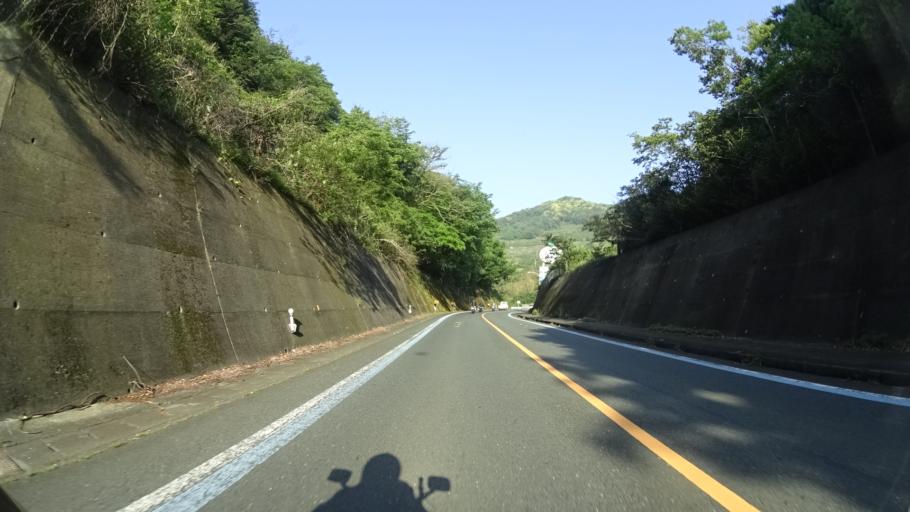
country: JP
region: Ehime
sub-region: Nishiuwa-gun
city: Ikata-cho
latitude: 33.4888
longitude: 132.3897
